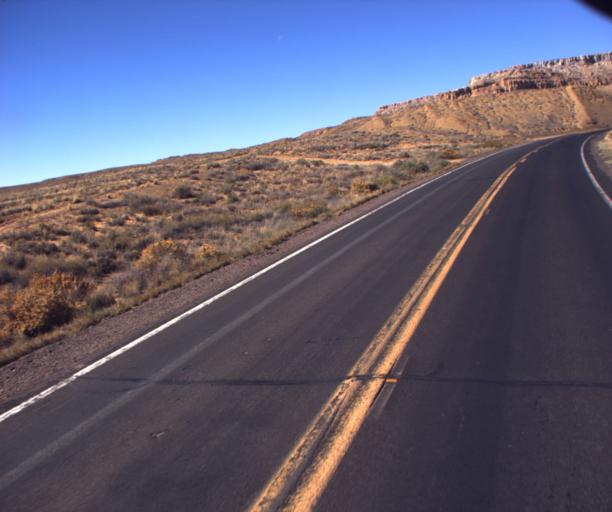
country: US
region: Arizona
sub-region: Navajo County
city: First Mesa
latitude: 35.7949
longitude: -110.5105
